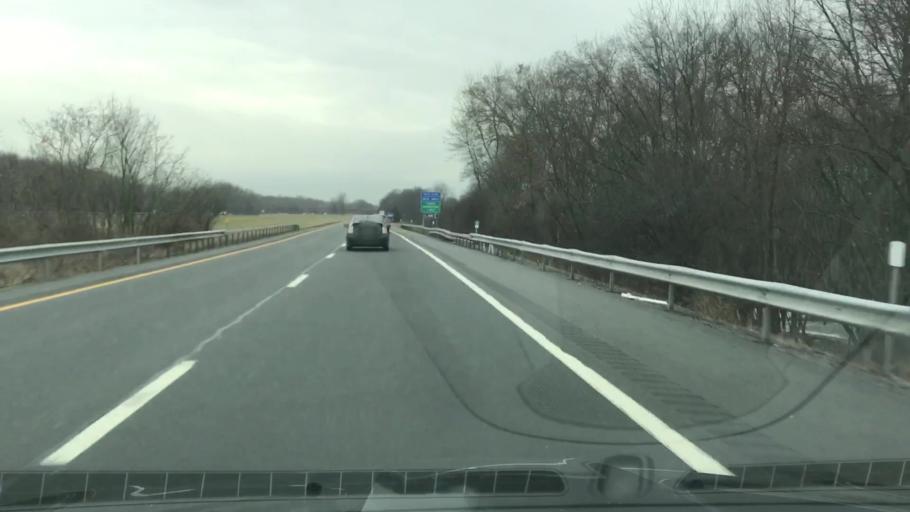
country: US
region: New York
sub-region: Orange County
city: Montgomery
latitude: 41.4902
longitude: -74.2750
